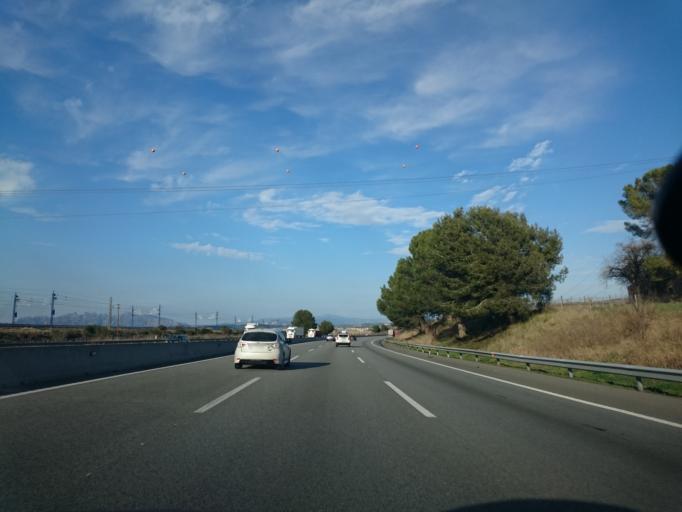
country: ES
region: Catalonia
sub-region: Provincia de Barcelona
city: La Granada
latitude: 41.3825
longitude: 1.7395
